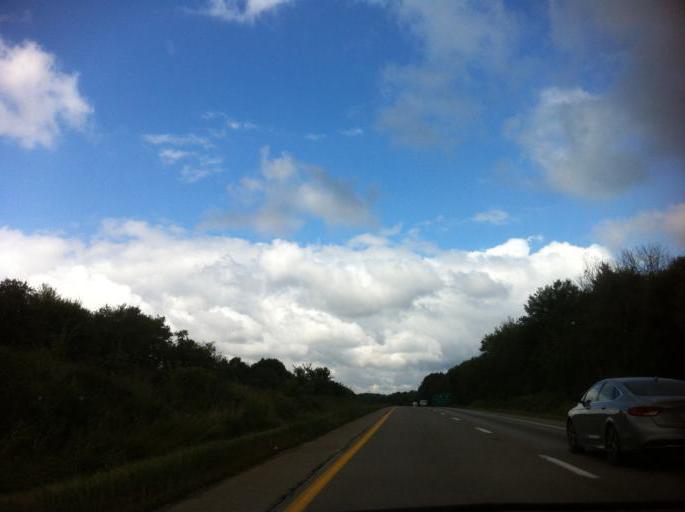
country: US
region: Pennsylvania
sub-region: Mercer County
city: Hermitage
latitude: 41.1833
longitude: -80.3974
